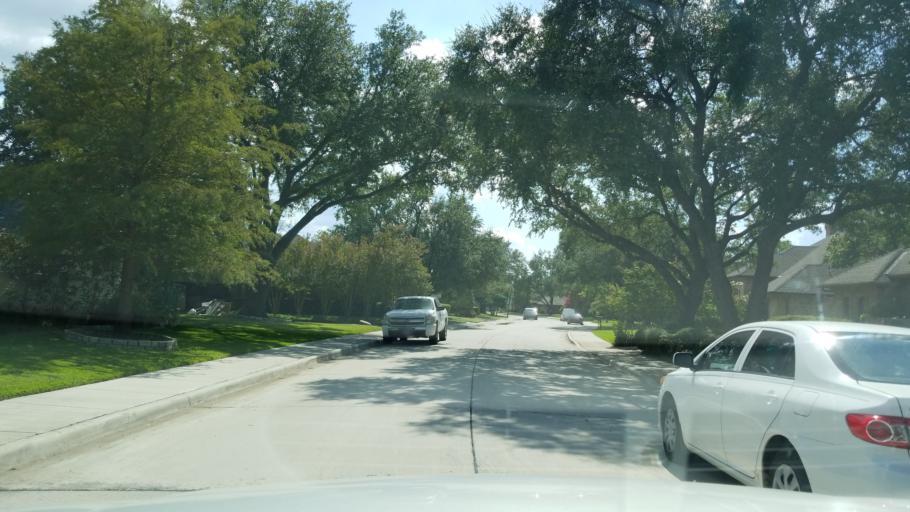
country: US
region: Texas
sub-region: Dallas County
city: Addison
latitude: 32.9613
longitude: -96.8016
